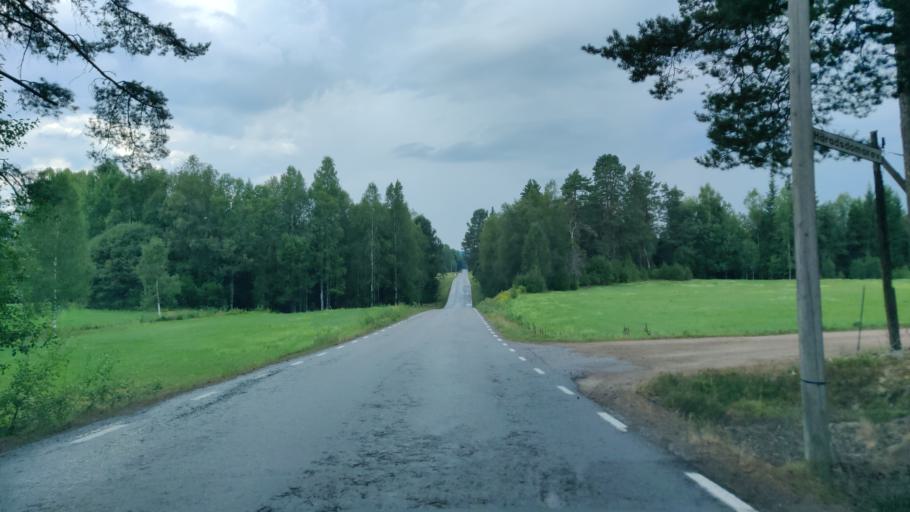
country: SE
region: Vaermland
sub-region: Munkfors Kommun
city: Munkfors
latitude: 59.8681
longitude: 13.5398
